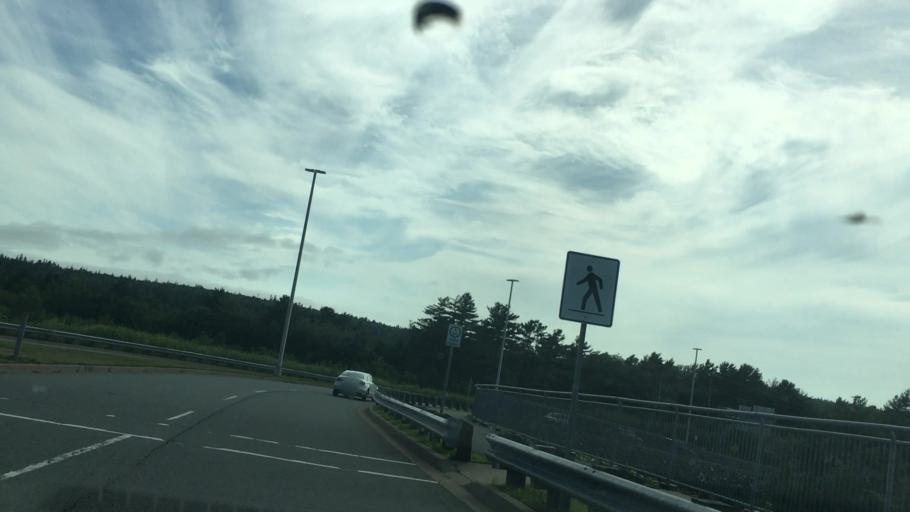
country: CA
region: Nova Scotia
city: Dartmouth
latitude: 44.6985
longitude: -63.6924
